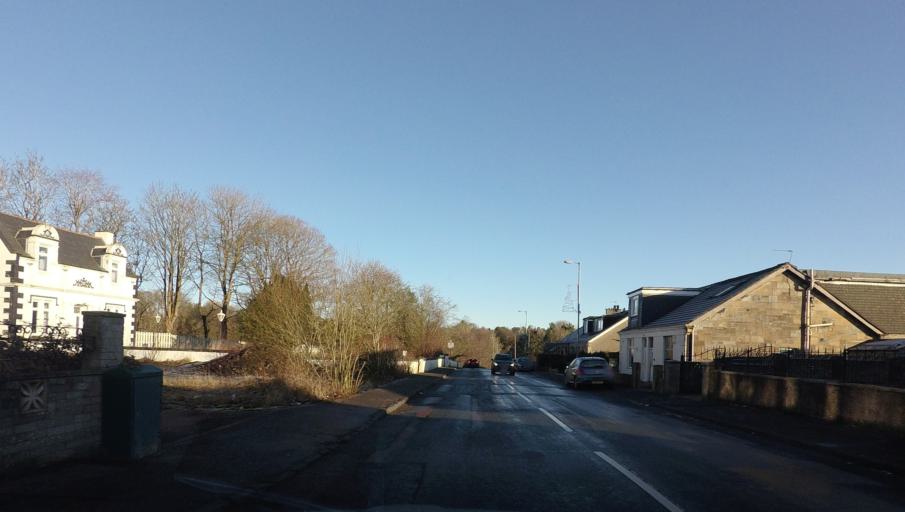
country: GB
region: Scotland
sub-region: North Lanarkshire
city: Newmains
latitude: 55.7887
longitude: -3.8650
